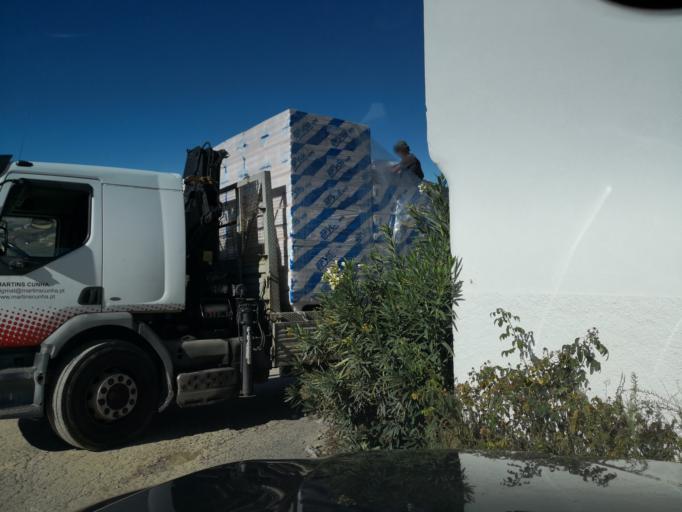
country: PT
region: Viseu
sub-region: Tabuaco
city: Tabuaco
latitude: 41.1768
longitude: -7.5154
